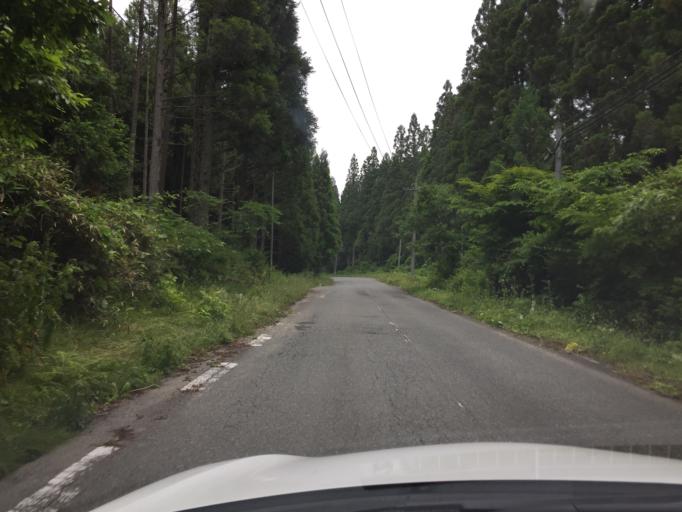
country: JP
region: Fukushima
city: Iwaki
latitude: 37.1703
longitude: 140.7115
